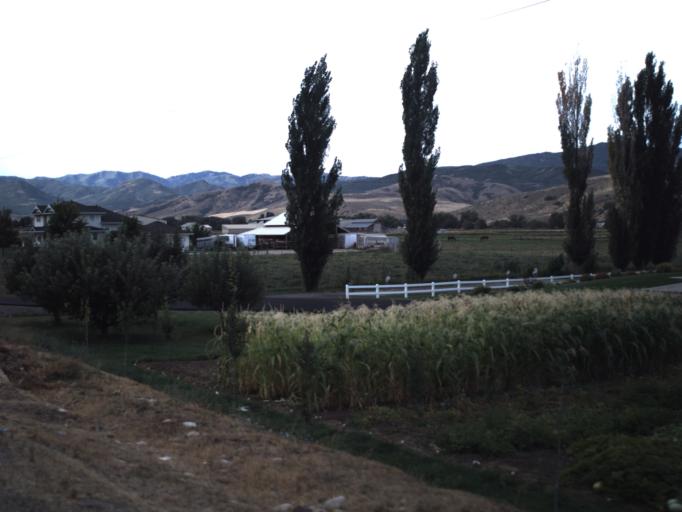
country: US
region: Utah
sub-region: Morgan County
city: Morgan
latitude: 41.0250
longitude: -111.6753
